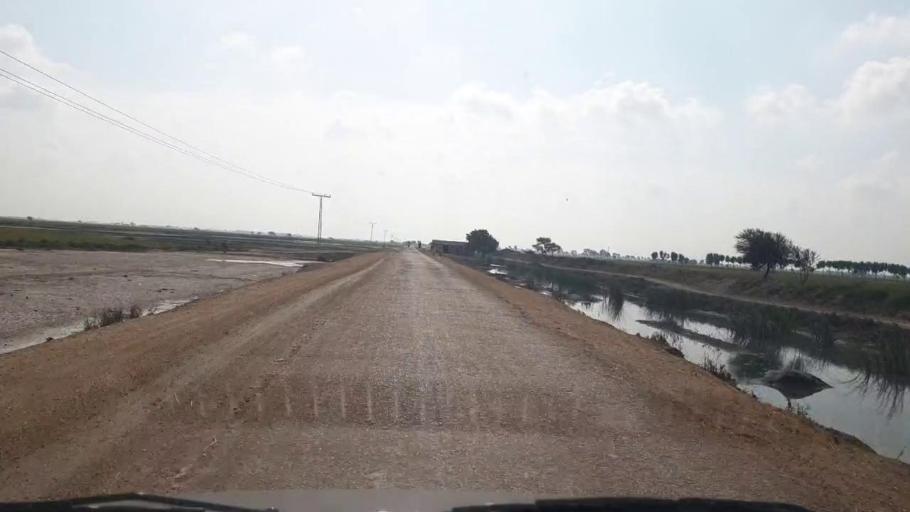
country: PK
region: Sindh
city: Kario
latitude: 24.6267
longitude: 68.5532
